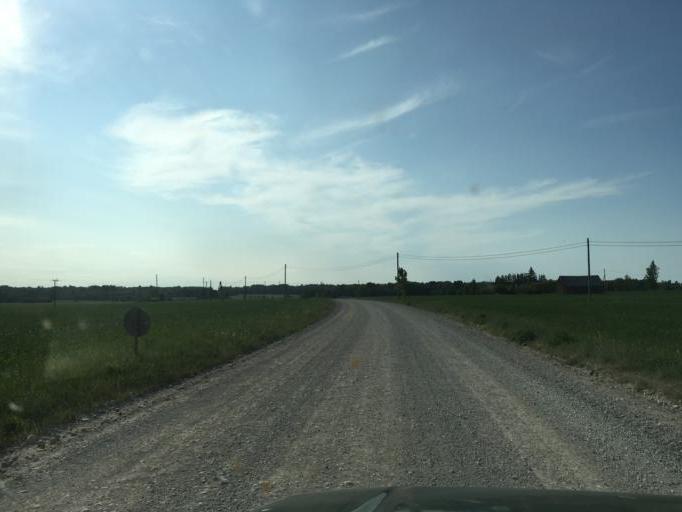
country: LV
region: Dundaga
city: Dundaga
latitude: 57.6225
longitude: 22.4085
